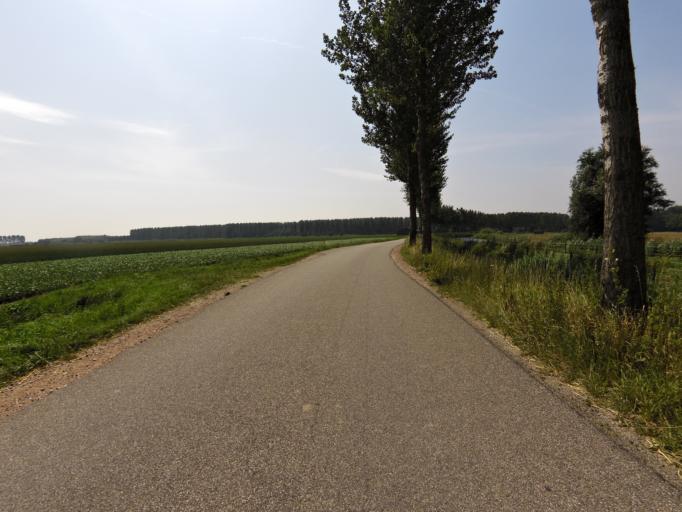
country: NL
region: South Holland
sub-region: Gemeente Dordrecht
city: Dordrecht
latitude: 51.7620
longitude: 4.7022
